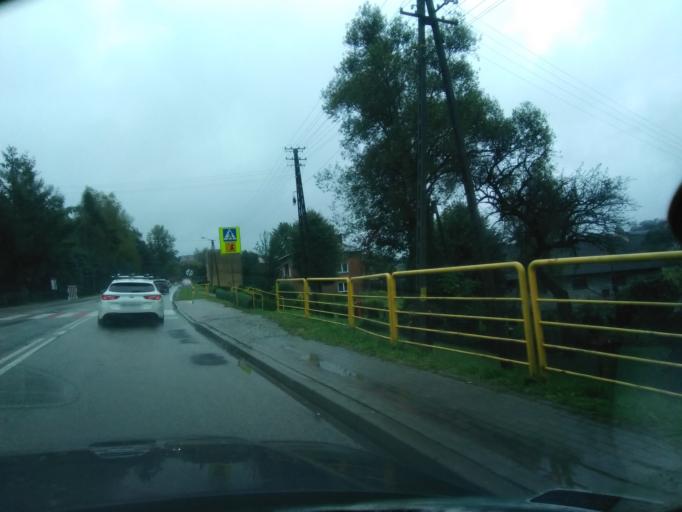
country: PL
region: Subcarpathian Voivodeship
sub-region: Powiat ropczycko-sedziszowski
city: Wielopole Skrzynskie
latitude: 49.9740
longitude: 21.5761
